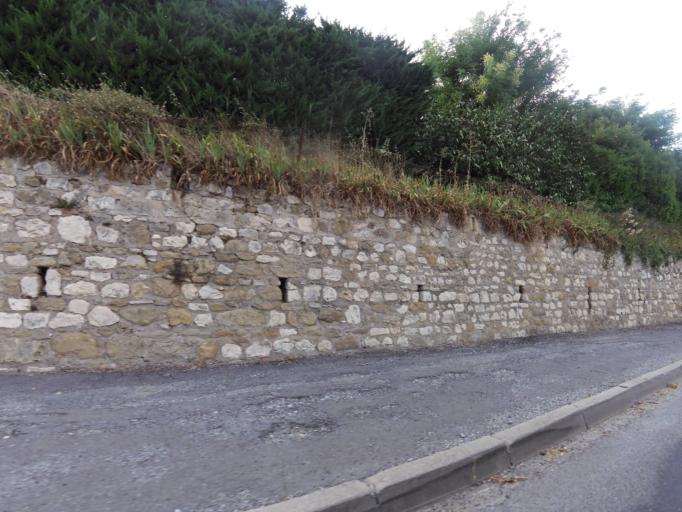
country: FR
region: Languedoc-Roussillon
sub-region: Departement du Gard
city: Saint-Genies-de-Malgoires
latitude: 43.9606
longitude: 4.2123
